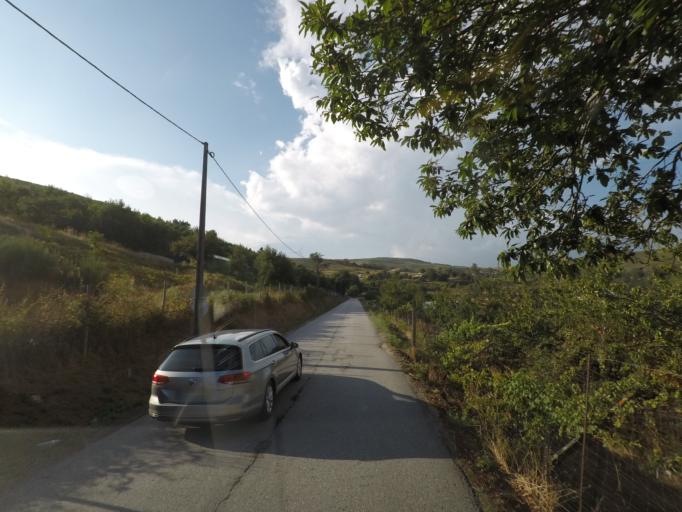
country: PT
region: Porto
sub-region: Baiao
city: Valadares
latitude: 41.1728
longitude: -7.9425
